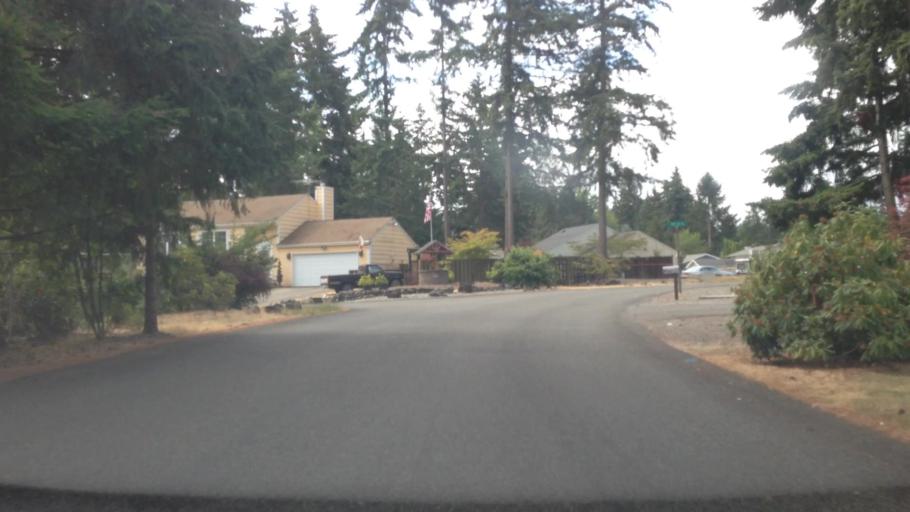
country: US
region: Washington
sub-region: Pierce County
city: South Hill
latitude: 47.1140
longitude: -122.3021
